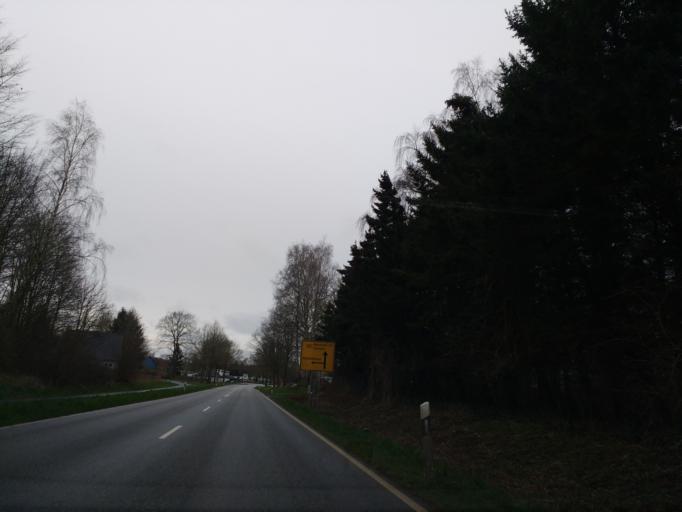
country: DE
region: Schleswig-Holstein
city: Grube
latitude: 54.2000
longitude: 11.0278
